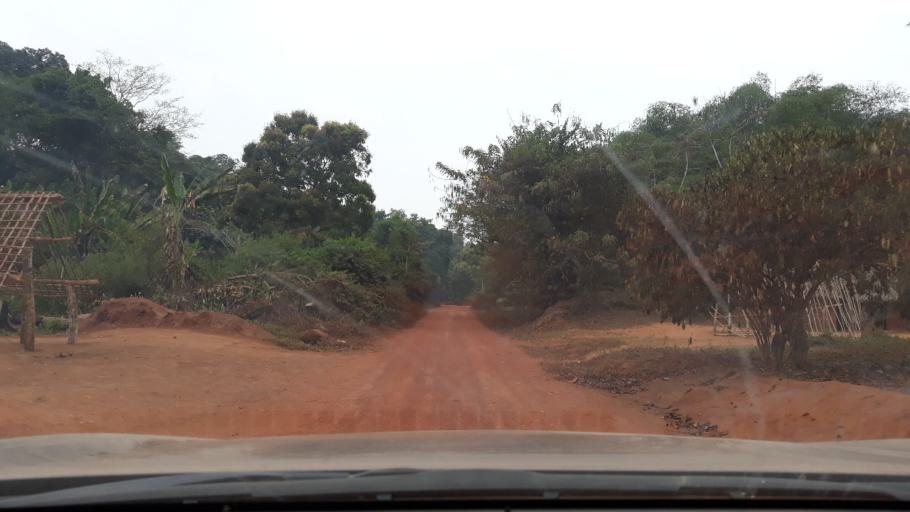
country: CD
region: Eastern Province
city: Buta
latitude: 2.2959
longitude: 25.0501
